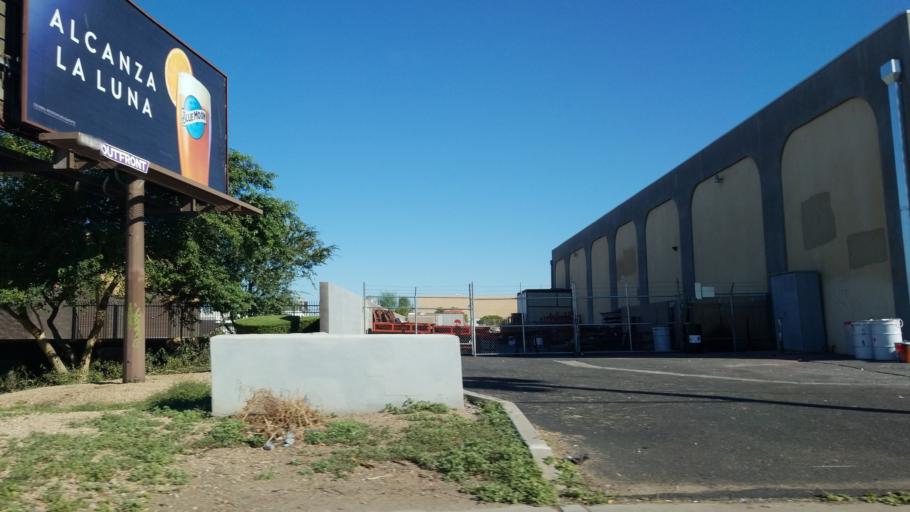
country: US
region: Arizona
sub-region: Maricopa County
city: Glendale
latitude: 33.5241
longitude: -112.1745
